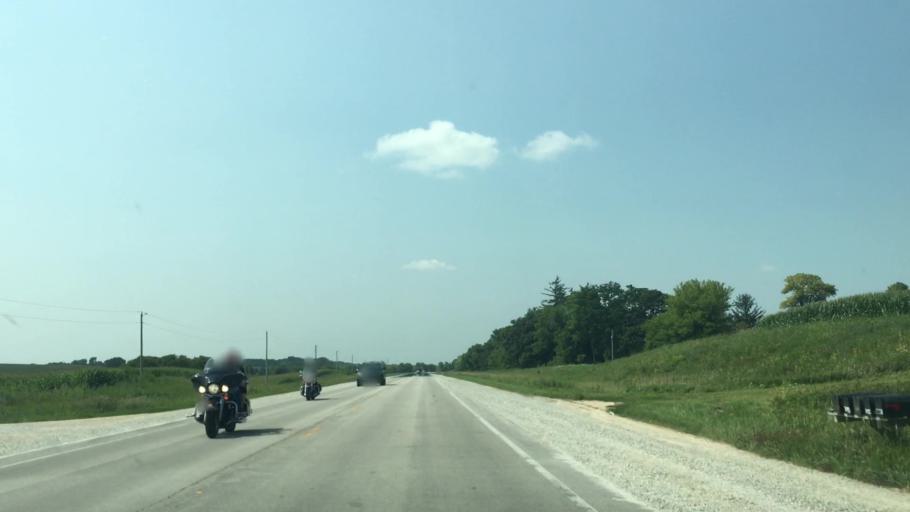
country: US
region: Iowa
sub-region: Winneshiek County
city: Decorah
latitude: 43.3999
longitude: -91.8437
